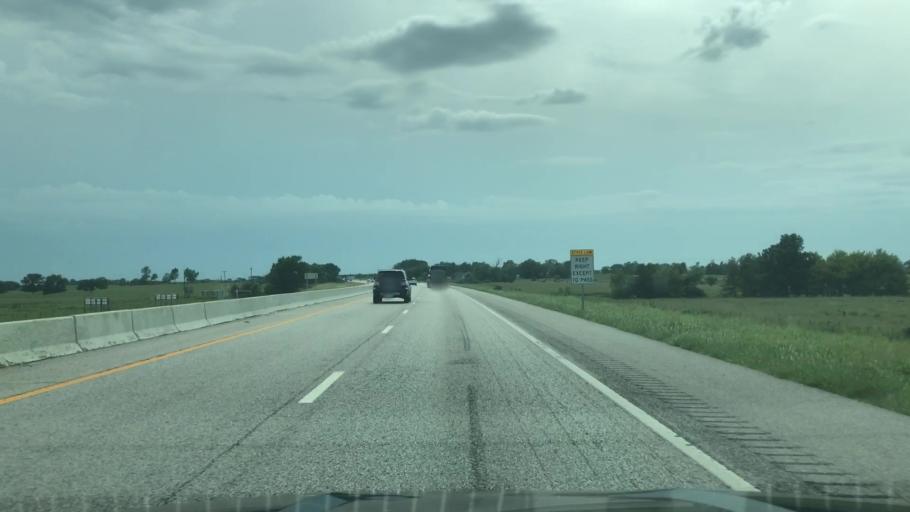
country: US
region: Oklahoma
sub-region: Craig County
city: Vinita
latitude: 36.6145
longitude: -95.1721
